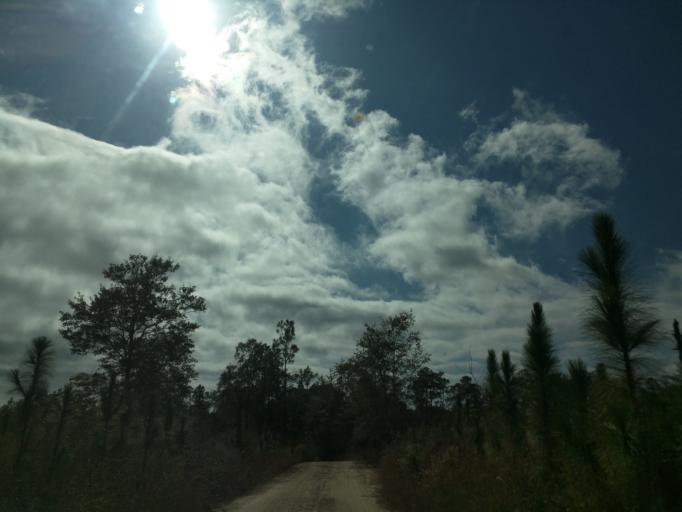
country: US
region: Florida
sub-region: Escambia County
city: Cantonment
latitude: 30.5467
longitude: -87.4307
